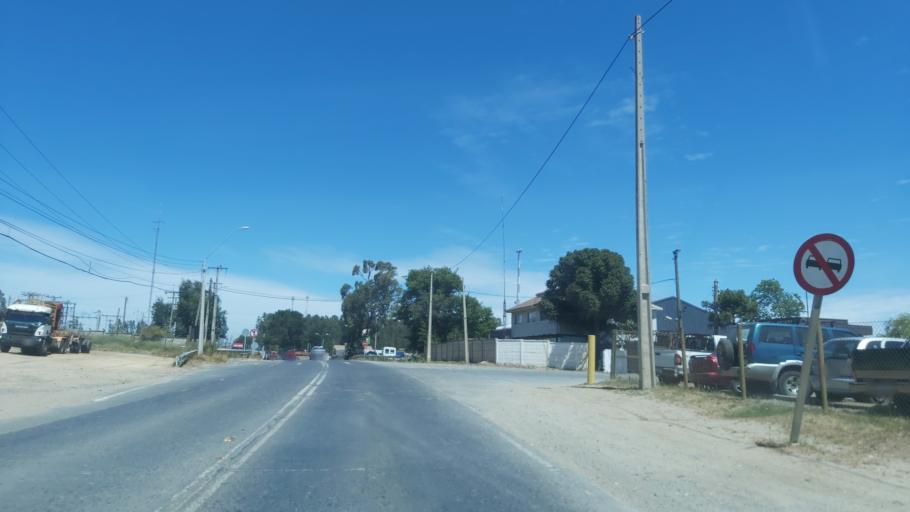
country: CL
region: Maule
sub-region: Provincia de Talca
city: Constitucion
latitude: -35.3626
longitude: -72.4044
